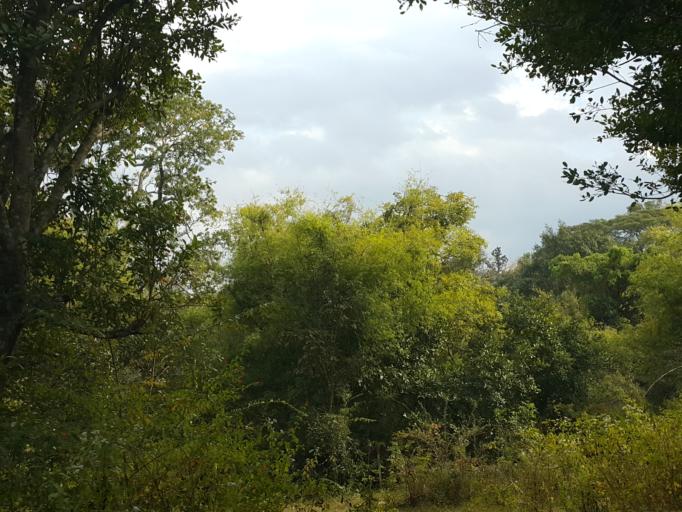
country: TH
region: Chiang Mai
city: Om Koi
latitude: 17.7950
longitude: 98.3398
